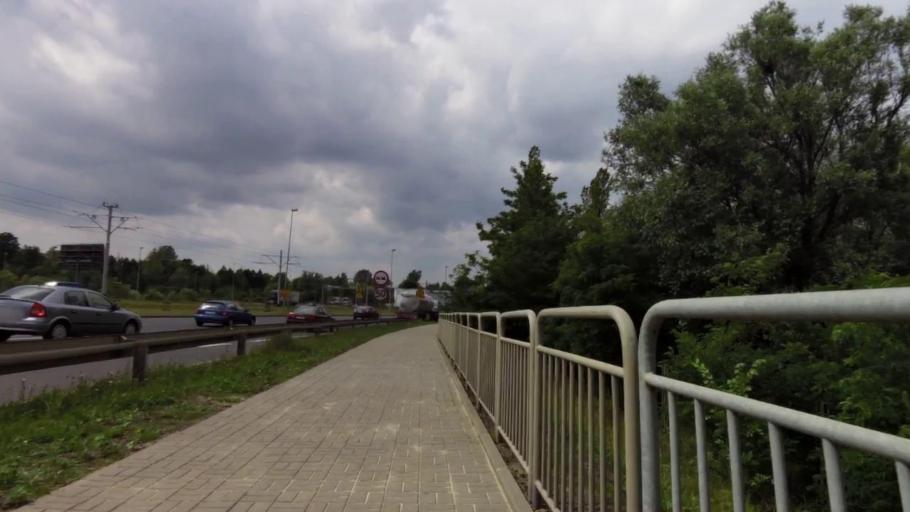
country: PL
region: West Pomeranian Voivodeship
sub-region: Szczecin
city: Szczecin
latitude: 53.3977
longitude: 14.6017
